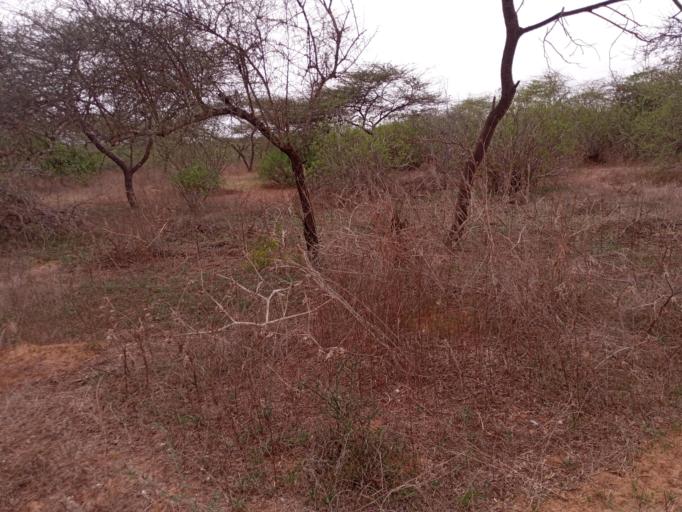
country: SN
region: Saint-Louis
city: Saint-Louis
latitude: 15.9232
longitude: -16.4533
